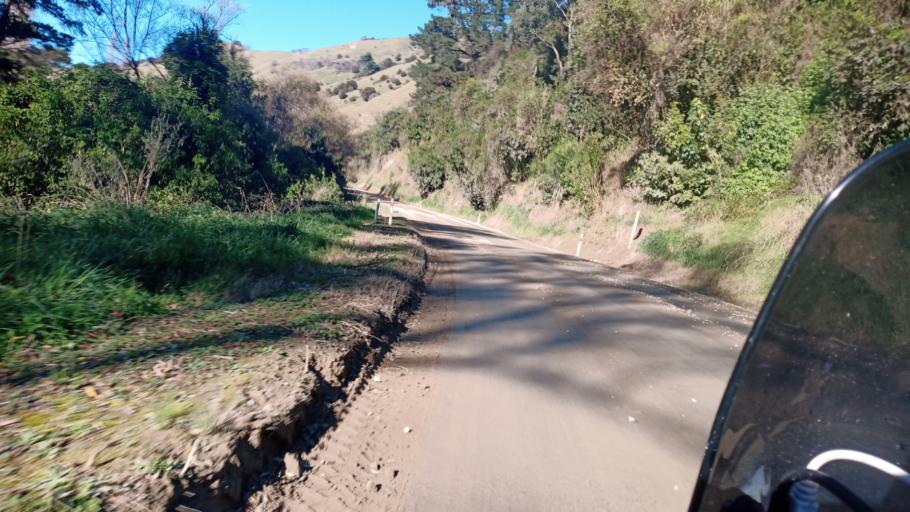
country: NZ
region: Hawke's Bay
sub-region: Wairoa District
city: Wairoa
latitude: -38.8462
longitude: 177.1659
